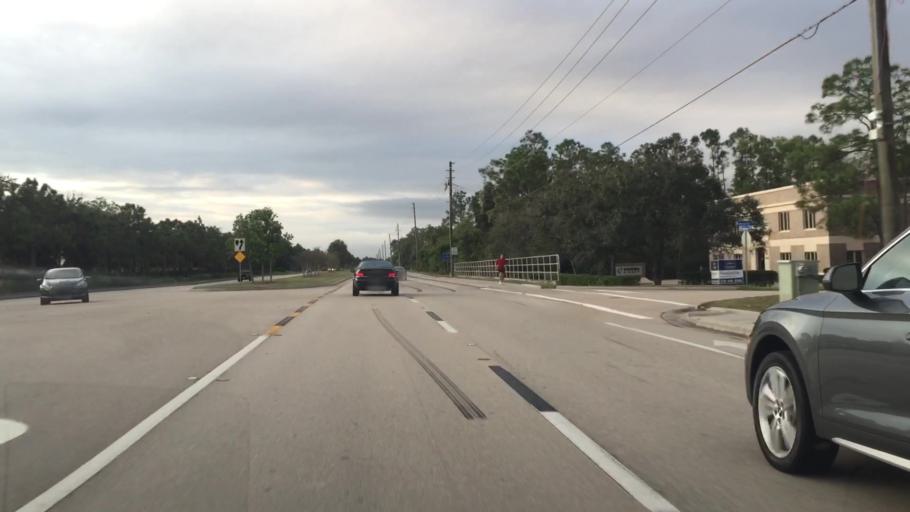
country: US
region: Florida
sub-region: Lee County
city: Gateway
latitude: 26.5628
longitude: -81.7867
